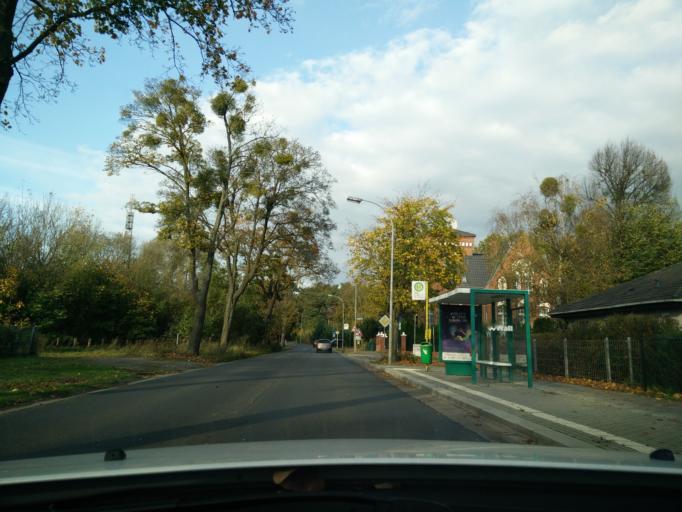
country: DE
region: Brandenburg
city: Falkensee
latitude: 52.5753
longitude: 13.1058
